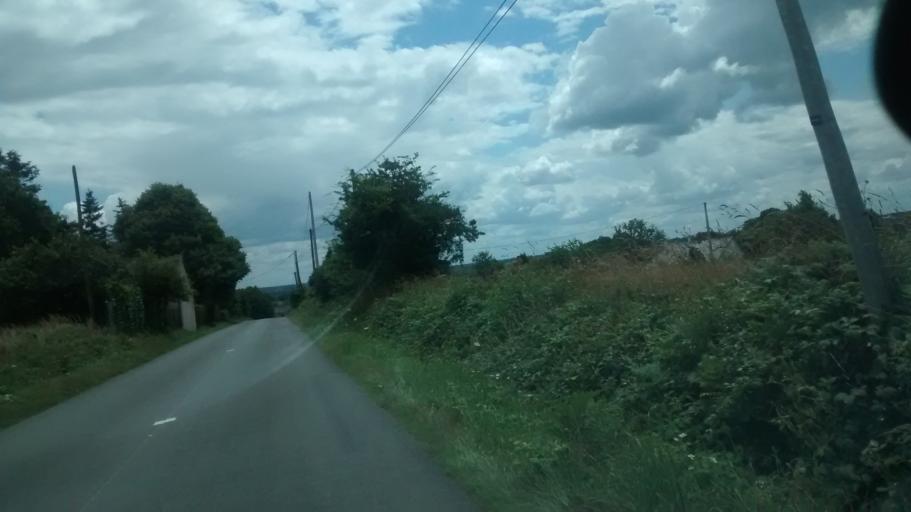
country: FR
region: Brittany
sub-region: Departement d'Ille-et-Vilaine
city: La Dominelais
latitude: 47.7870
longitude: -1.7069
